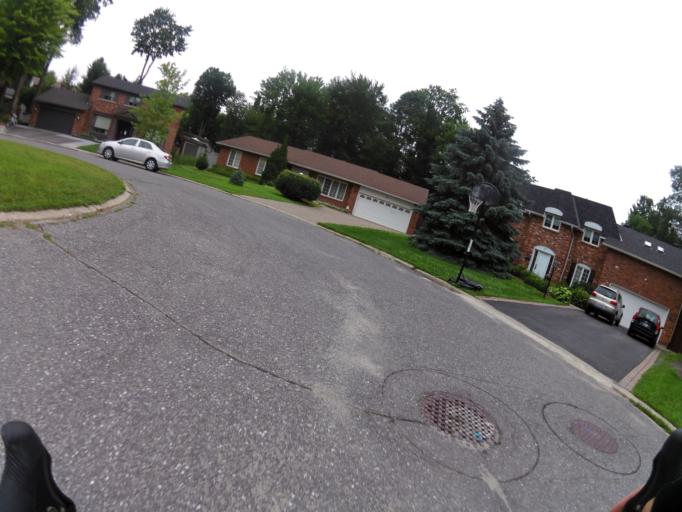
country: CA
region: Ontario
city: Ottawa
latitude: 45.3203
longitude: -75.7125
